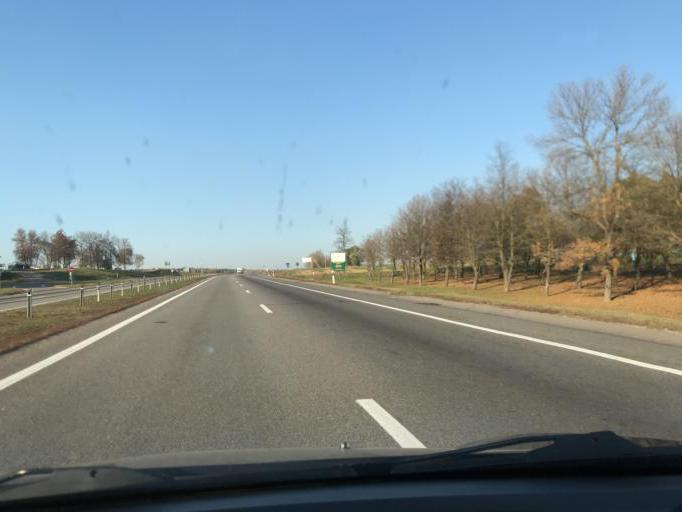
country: BY
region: Minsk
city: Samakhvalavichy
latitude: 53.7477
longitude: 27.5143
